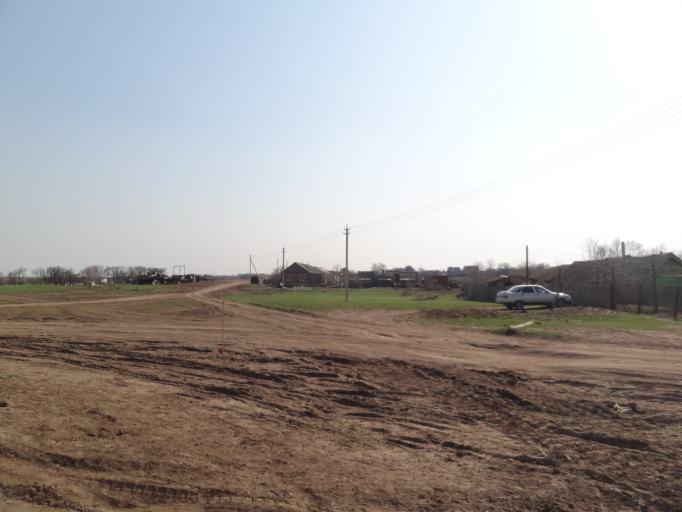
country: RU
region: Saratov
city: Privolzhskiy
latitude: 51.3243
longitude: 45.9781
